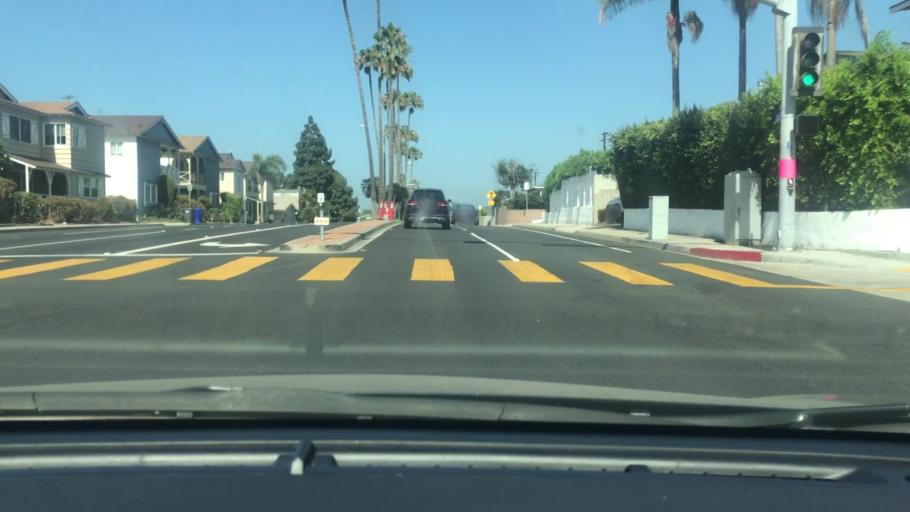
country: US
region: California
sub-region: Los Angeles County
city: Manhattan Beach
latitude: 33.8874
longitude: -118.3917
